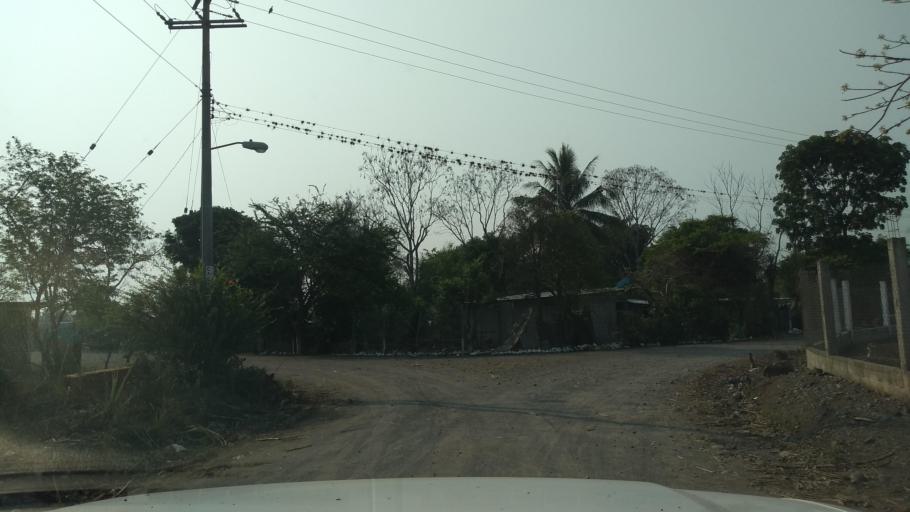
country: MX
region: Oaxaca
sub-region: Cosolapa
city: Cosolapa
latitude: 18.6242
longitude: -96.6075
